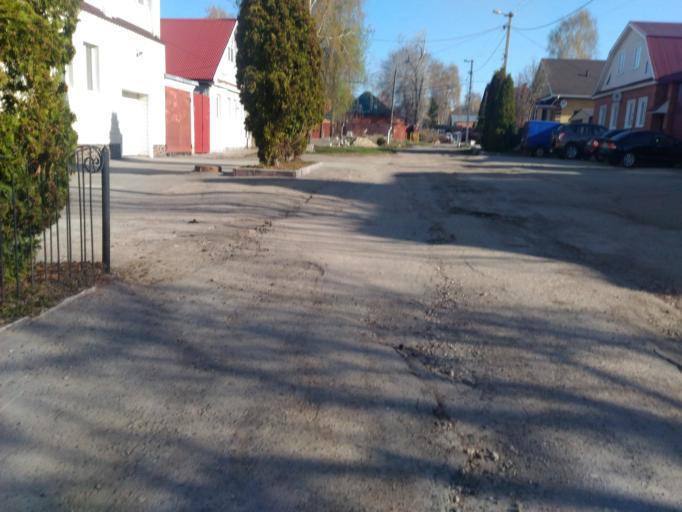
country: RU
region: Ulyanovsk
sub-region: Ulyanovskiy Rayon
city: Ulyanovsk
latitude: 54.3399
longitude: 48.3877
